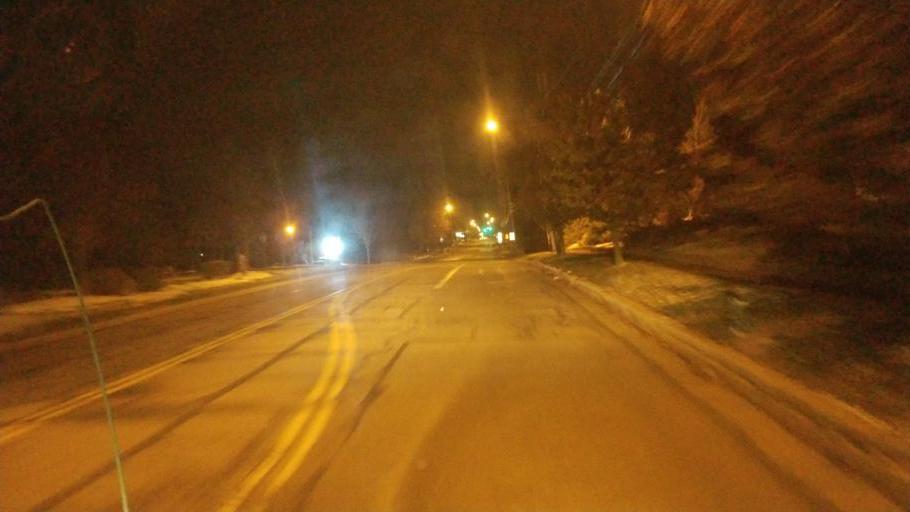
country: US
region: Ohio
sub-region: Cuyahoga County
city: Oakwood
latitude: 41.3604
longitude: -81.5022
